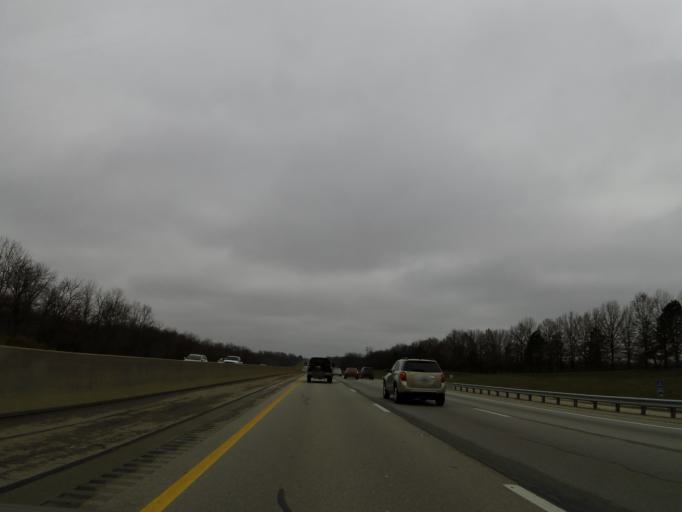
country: US
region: Kentucky
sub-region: Grant County
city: Crittenden
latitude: 38.8170
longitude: -84.6011
